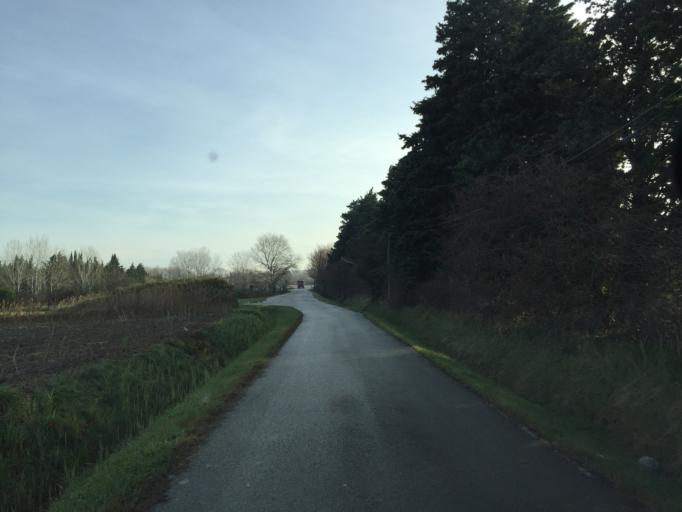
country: FR
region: Provence-Alpes-Cote d'Azur
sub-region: Departement du Vaucluse
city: Orange
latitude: 44.1335
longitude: 4.7804
